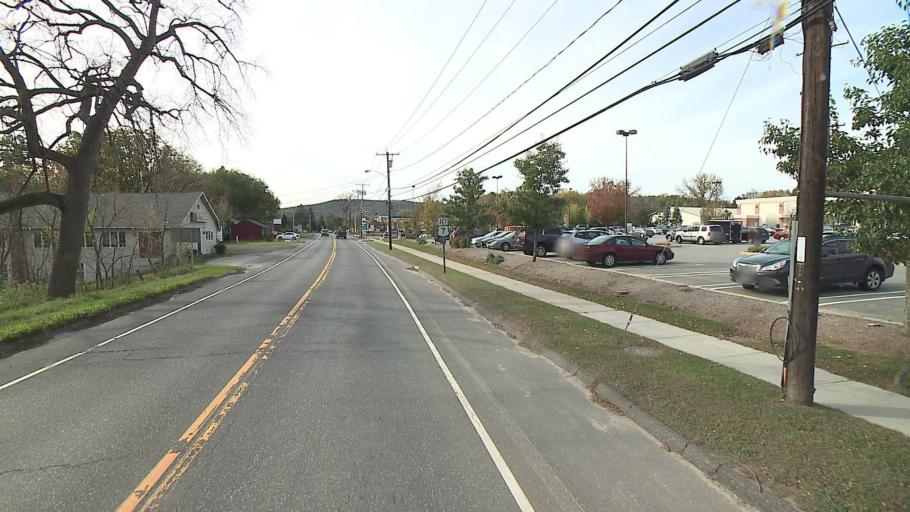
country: US
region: Connecticut
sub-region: Litchfield County
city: Canaan
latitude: 42.0238
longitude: -73.3219
